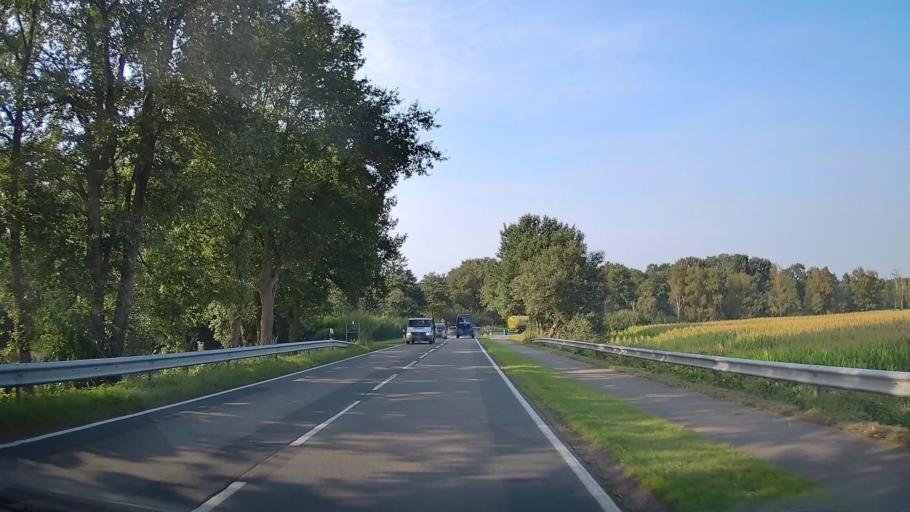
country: DE
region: Lower Saxony
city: Friesoythe
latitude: 53.0853
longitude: 7.8314
